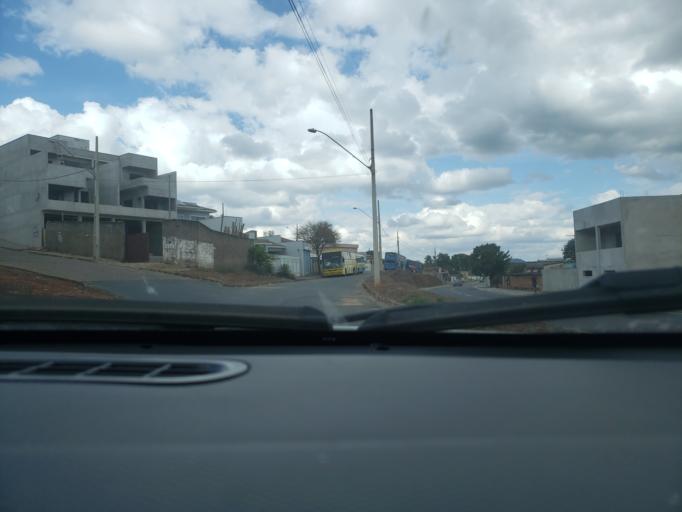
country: BR
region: Minas Gerais
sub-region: Campo Belo
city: Campo Belo
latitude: -20.8951
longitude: -45.2676
